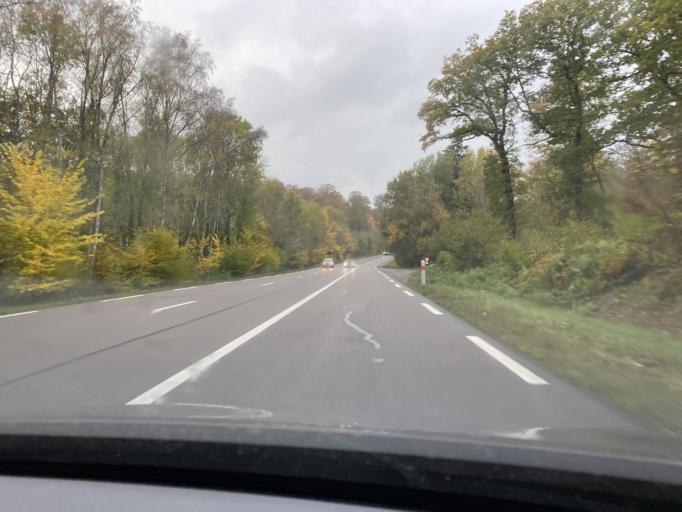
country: FR
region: Bourgogne
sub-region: Departement de la Cote-d'Or
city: Saulieu
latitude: 47.3005
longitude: 4.2118
